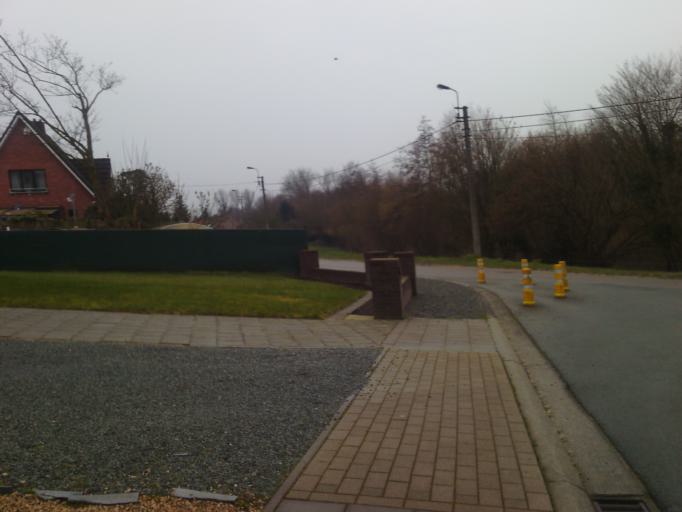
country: BE
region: Flanders
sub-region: Provincie Oost-Vlaanderen
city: Berlare
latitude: 51.0303
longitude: 4.0020
